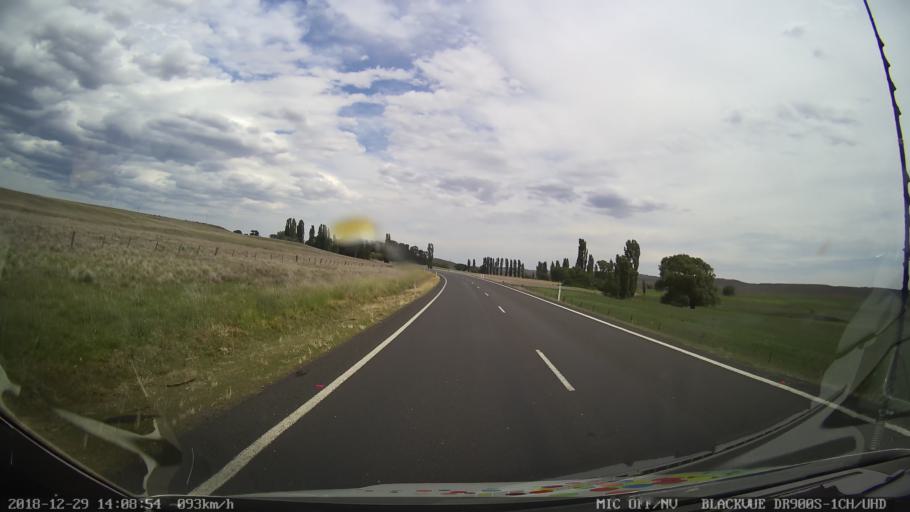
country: AU
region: New South Wales
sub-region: Cooma-Monaro
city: Cooma
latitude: -36.3715
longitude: 149.2126
